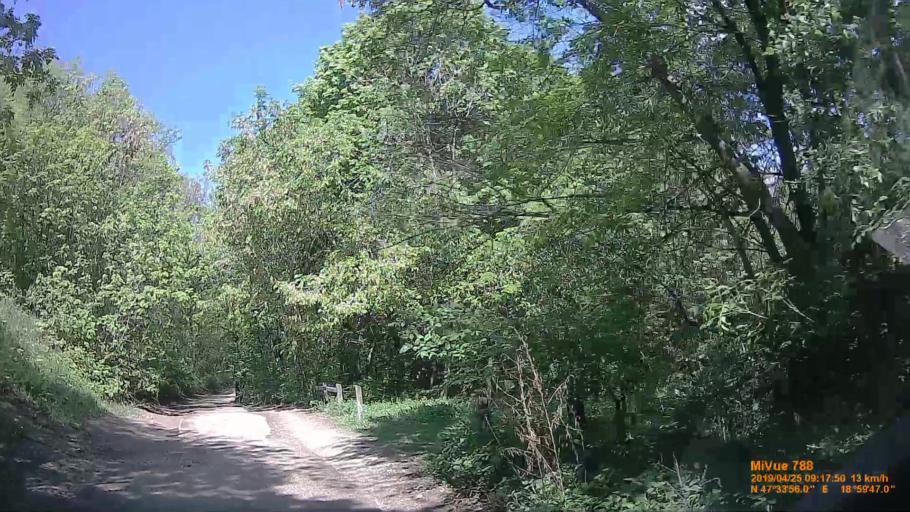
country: HU
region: Pest
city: Urom
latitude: 47.5656
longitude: 18.9964
